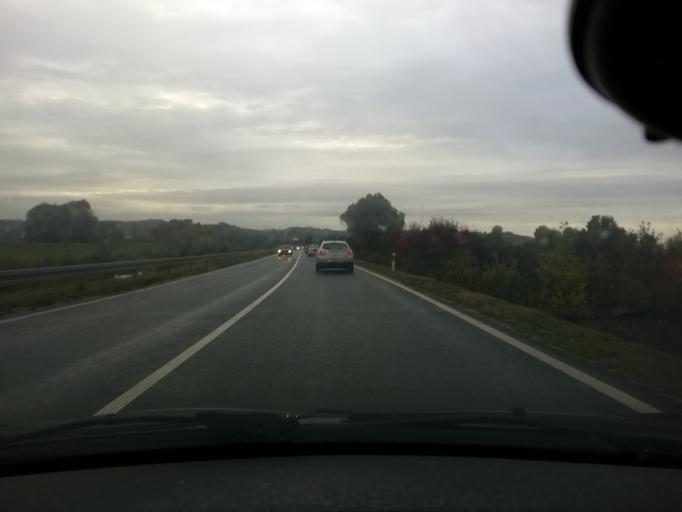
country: HR
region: Zagrebacka
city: Pojatno
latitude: 45.8943
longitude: 15.8198
